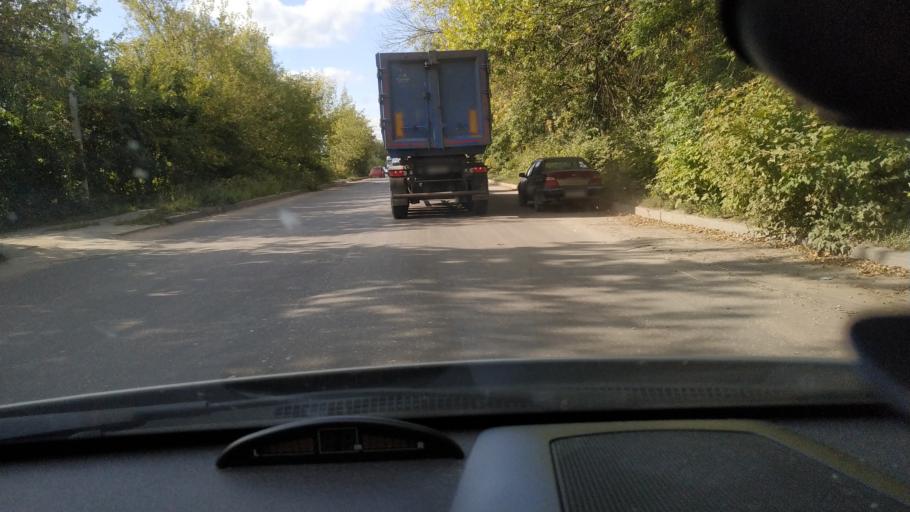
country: RU
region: Rjazan
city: Ryazan'
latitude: 54.6586
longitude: 39.6344
